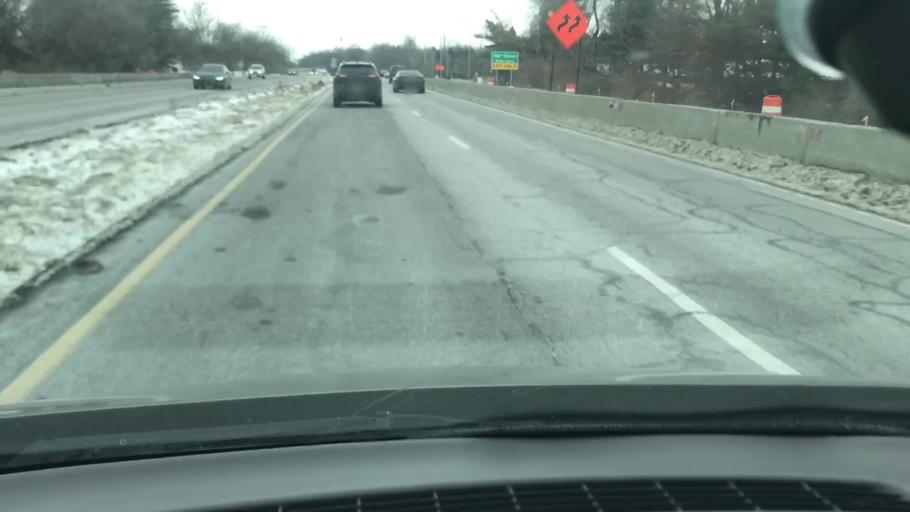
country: US
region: Indiana
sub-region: Hamilton County
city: Carmel
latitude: 39.9321
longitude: -86.1122
